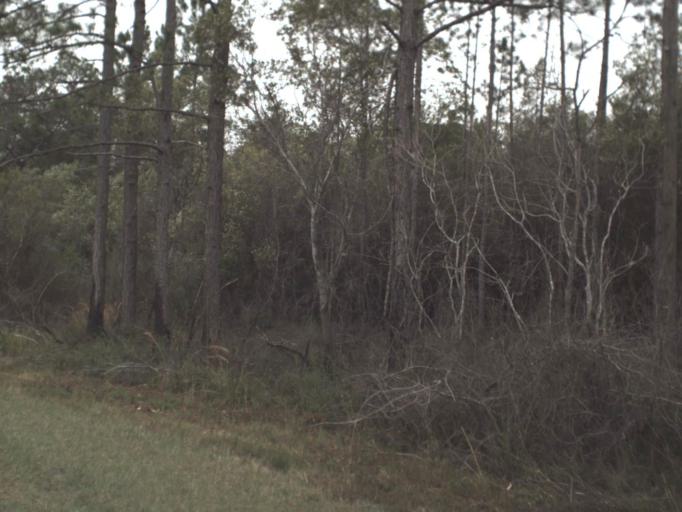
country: US
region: Florida
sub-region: Gulf County
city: Wewahitchka
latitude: 30.1325
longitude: -84.9881
